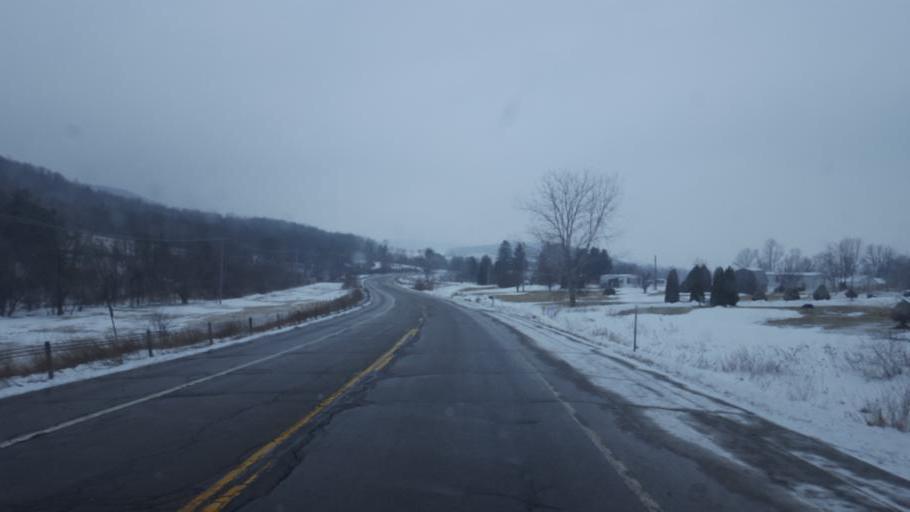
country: US
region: Pennsylvania
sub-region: Tioga County
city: Westfield
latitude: 42.1091
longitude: -77.4750
